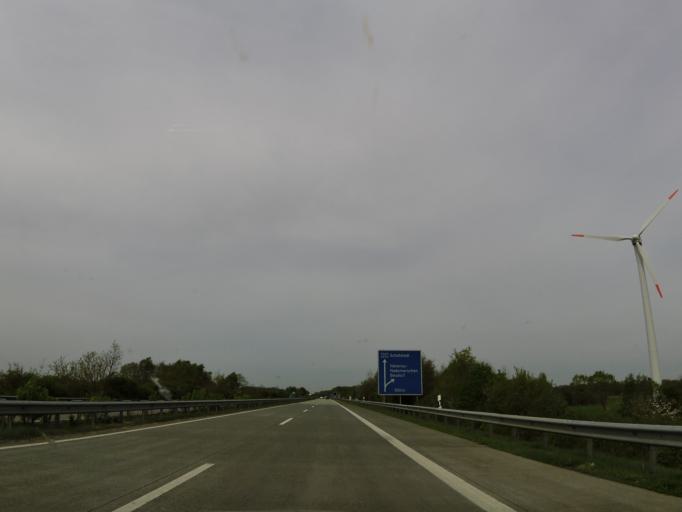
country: DE
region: Schleswig-Holstein
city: Besdorf
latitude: 54.0553
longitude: 9.3769
